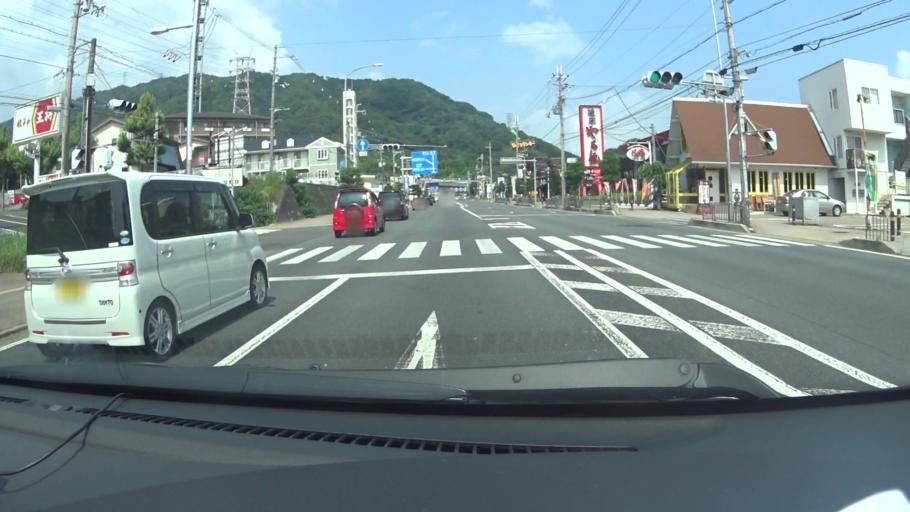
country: JP
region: Kyoto
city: Muko
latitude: 34.9750
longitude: 135.6622
